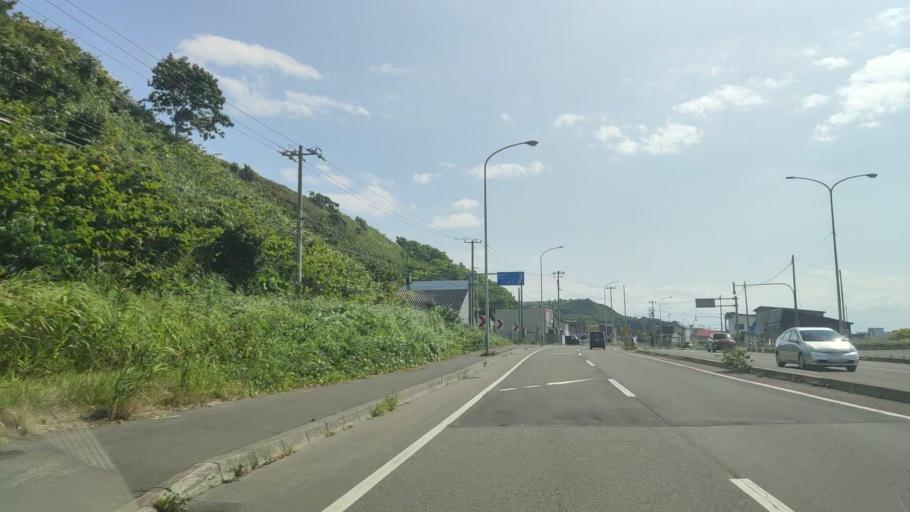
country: JP
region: Hokkaido
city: Rumoi
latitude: 44.0013
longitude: 141.6575
